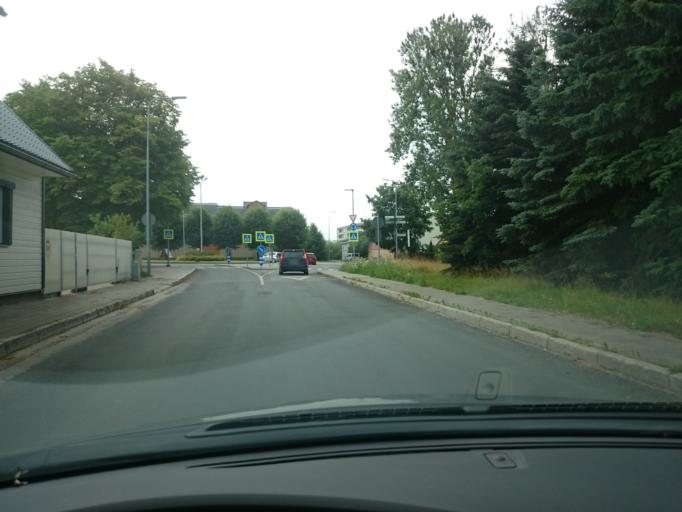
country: EE
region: Laeaene
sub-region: Haapsalu linn
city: Haapsalu
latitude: 58.9399
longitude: 23.5341
